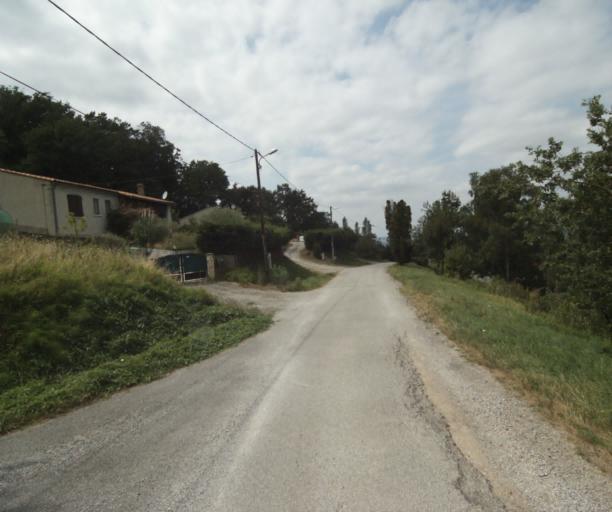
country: FR
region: Midi-Pyrenees
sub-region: Departement du Tarn
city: Soreze
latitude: 43.4374
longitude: 2.0450
